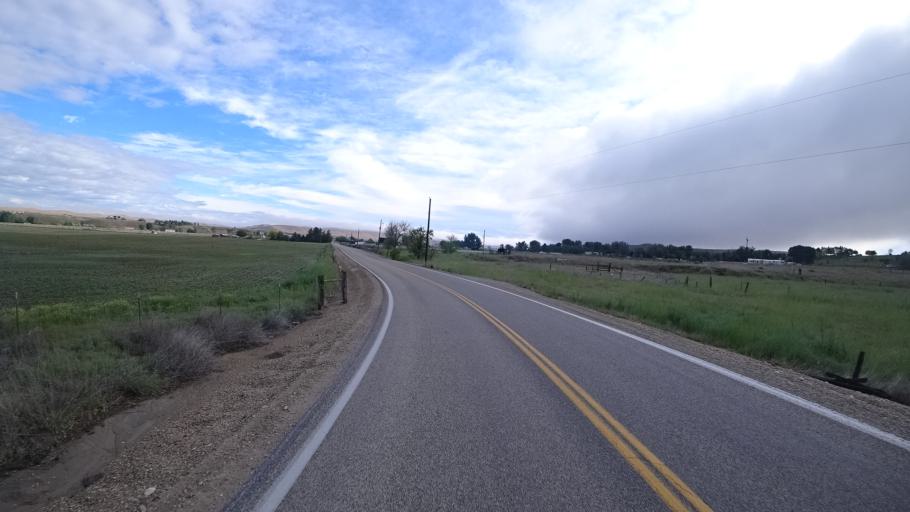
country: US
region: Idaho
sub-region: Ada County
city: Star
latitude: 43.7724
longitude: -116.4732
